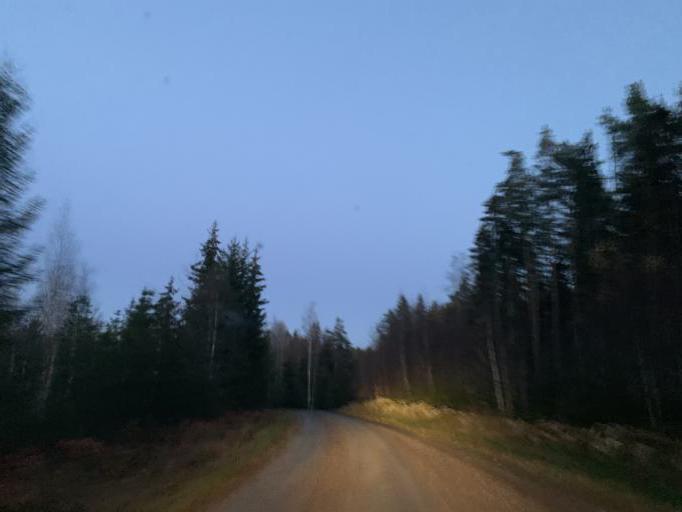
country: SE
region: OErebro
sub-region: Lindesbergs Kommun
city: Fellingsbro
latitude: 59.3748
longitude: 15.6209
